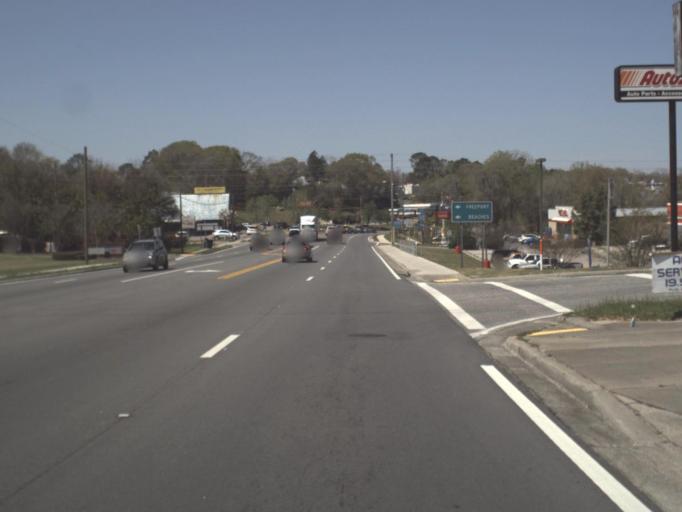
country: US
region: Florida
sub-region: Walton County
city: DeFuniak Springs
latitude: 30.7216
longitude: -86.1175
